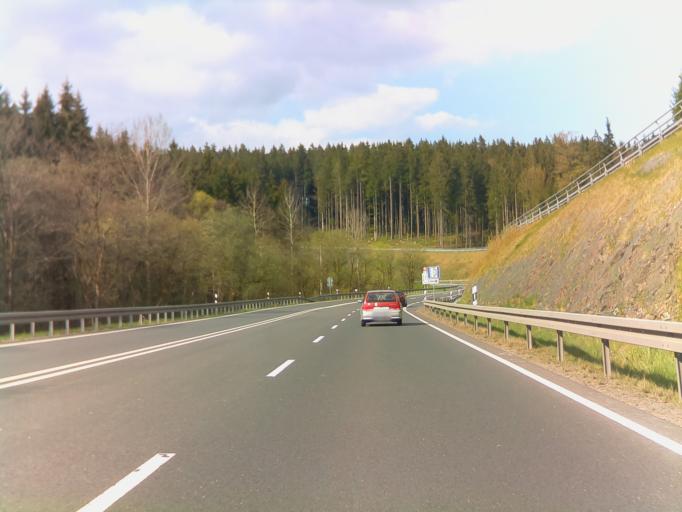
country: DE
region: Bavaria
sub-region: Upper Franconia
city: Teuschnitz
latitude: 50.4105
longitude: 11.3539
